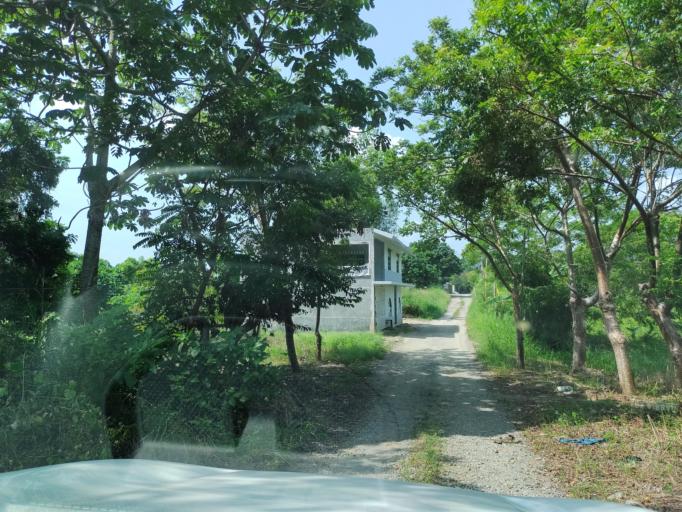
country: MX
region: Veracruz
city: Martinez de la Torre
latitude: 20.0877
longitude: -97.0541
